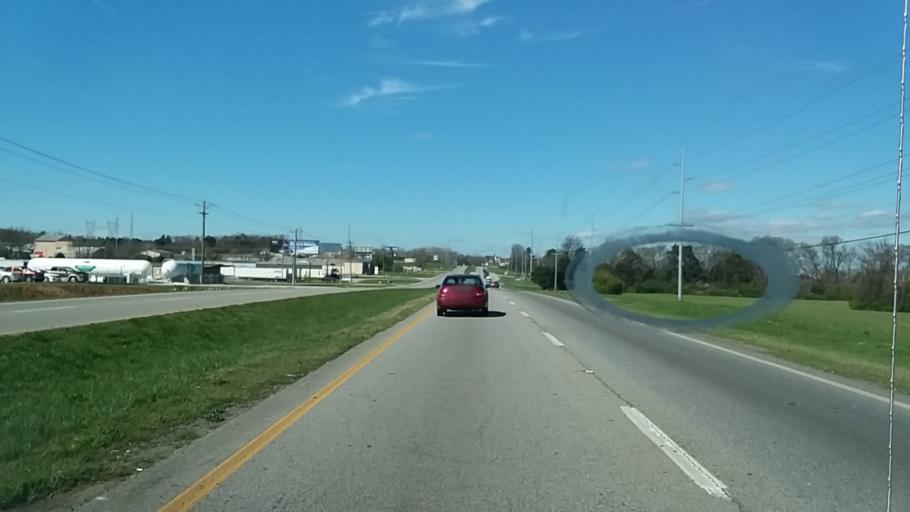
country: US
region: Alabama
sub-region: Morgan County
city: Trinity
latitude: 34.6199
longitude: -87.0609
